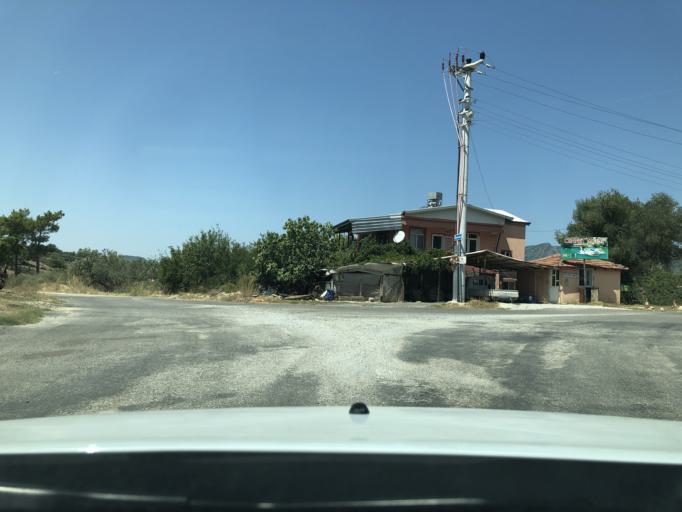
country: TR
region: Antalya
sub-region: Manavgat
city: Kizilagac
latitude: 36.8572
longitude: 31.5632
